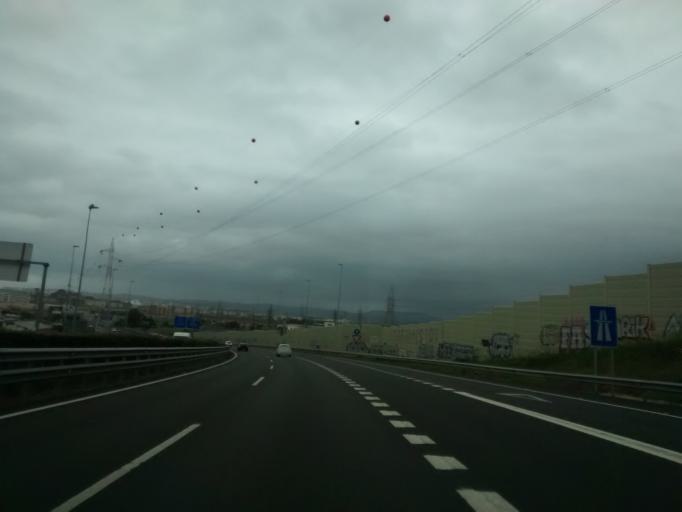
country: ES
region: Cantabria
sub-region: Provincia de Cantabria
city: Camargo
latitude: 43.4361
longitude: -3.8731
